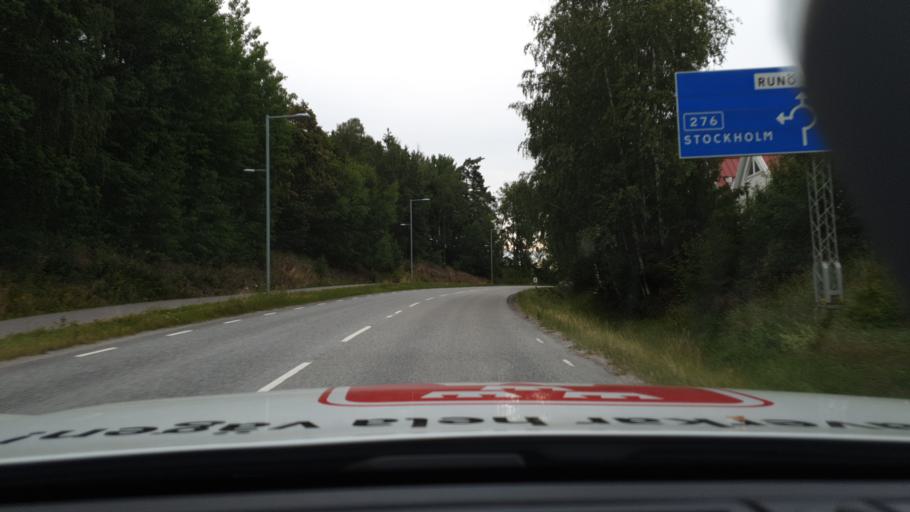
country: SE
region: Stockholm
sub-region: Osterakers Kommun
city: Akersberga
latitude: 59.4849
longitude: 18.2732
